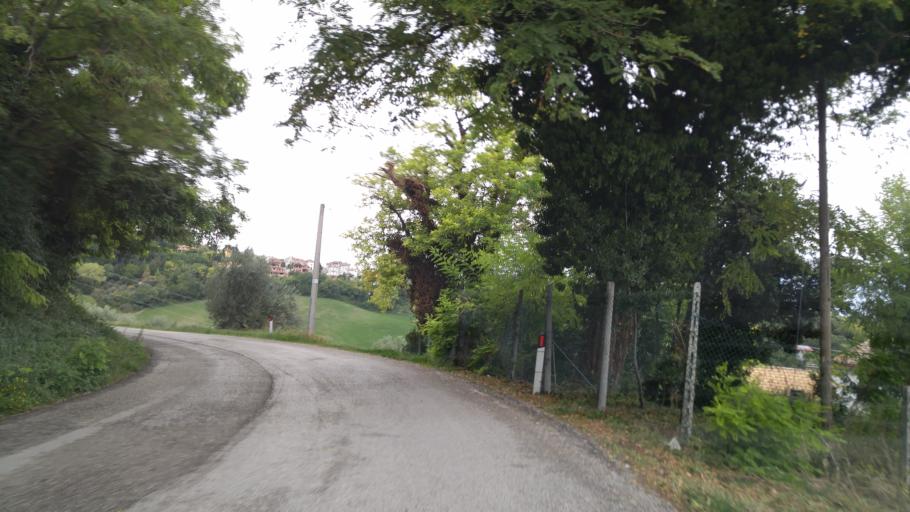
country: IT
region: The Marches
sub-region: Provincia di Pesaro e Urbino
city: Mombaroccio
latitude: 43.7950
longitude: 12.8722
